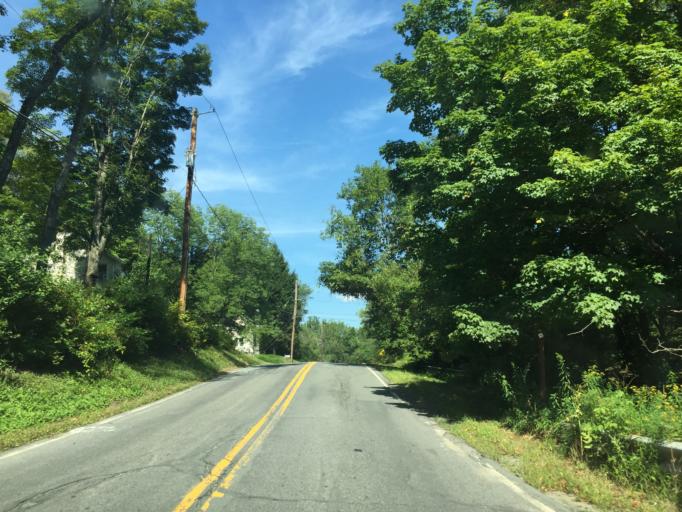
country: US
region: New York
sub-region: Sullivan County
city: Livingston Manor
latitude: 41.9254
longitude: -74.9086
